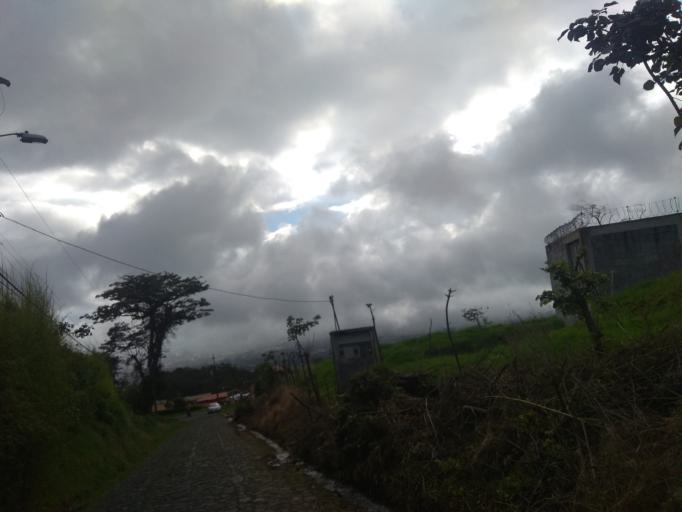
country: CR
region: San Jose
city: Ipis
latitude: 9.9864
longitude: -83.9585
